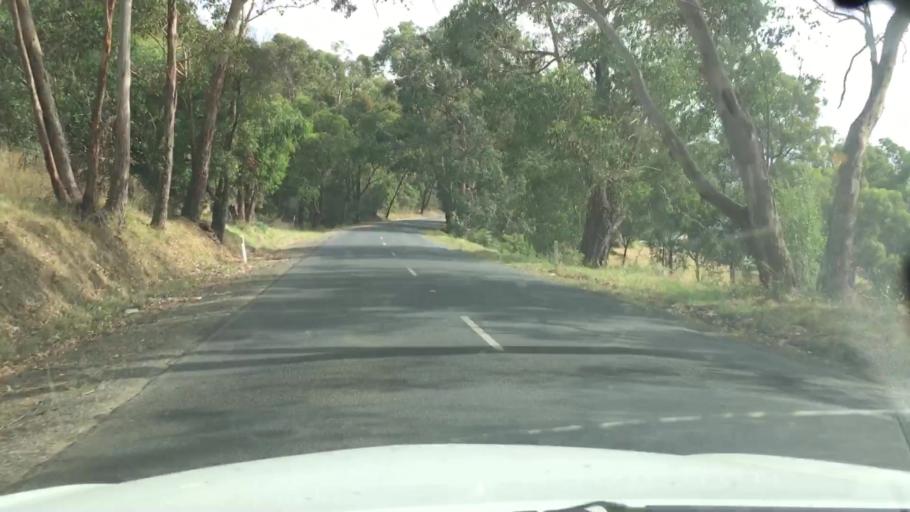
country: AU
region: Victoria
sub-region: Yarra Ranges
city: Macclesfield
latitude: -37.8813
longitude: 145.4770
